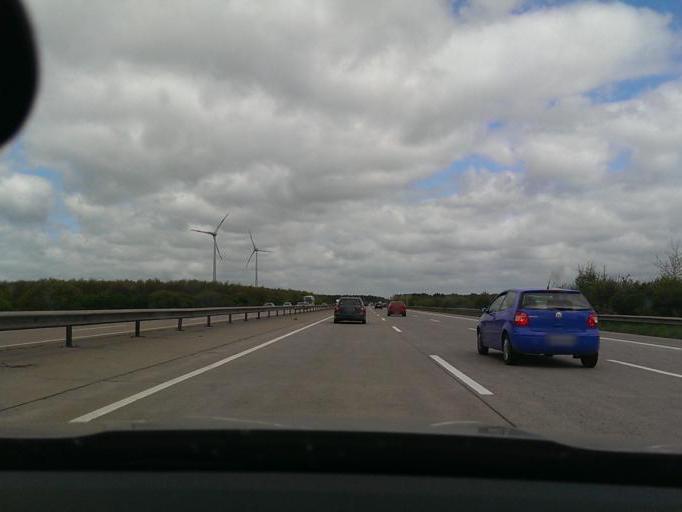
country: DE
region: Lower Saxony
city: Lindwedel
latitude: 52.6489
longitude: 9.7074
